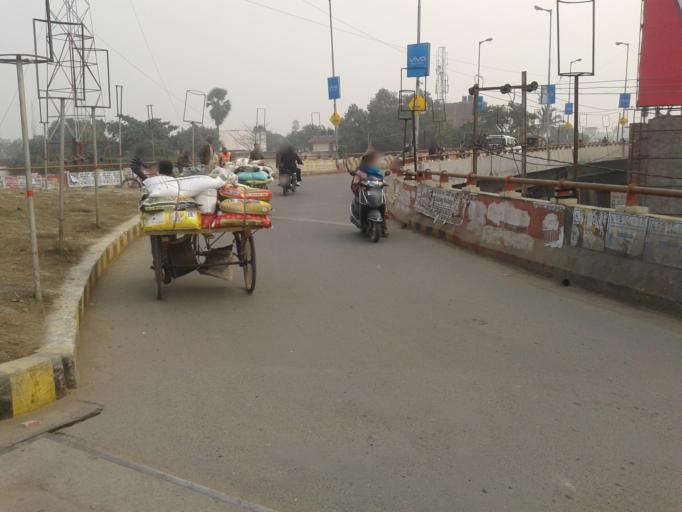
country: IN
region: Bihar
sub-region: Muzaffarpur
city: Muzaffarpur
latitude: 26.1199
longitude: 85.3855
